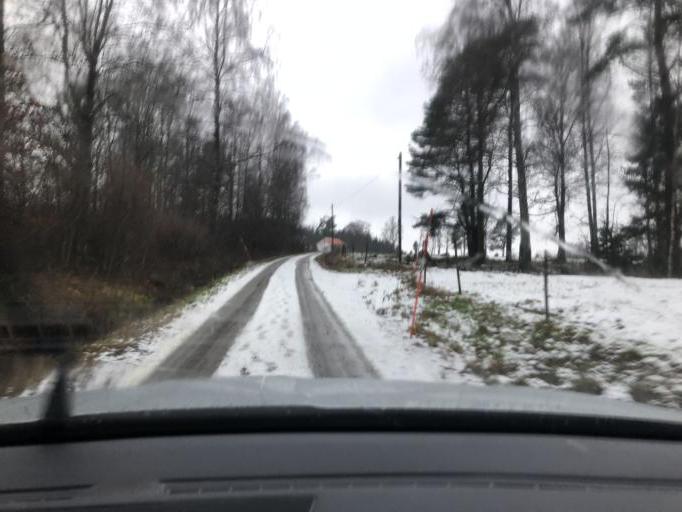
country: SE
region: Vaestra Goetaland
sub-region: Ulricehamns Kommun
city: Ulricehamn
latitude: 57.8237
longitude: 13.2800
